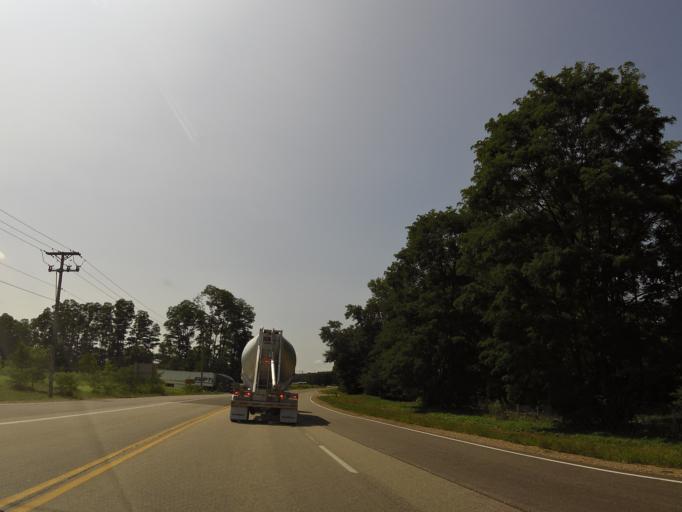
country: US
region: Wisconsin
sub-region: Columbia County
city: Poynette
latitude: 43.3903
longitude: -89.4706
